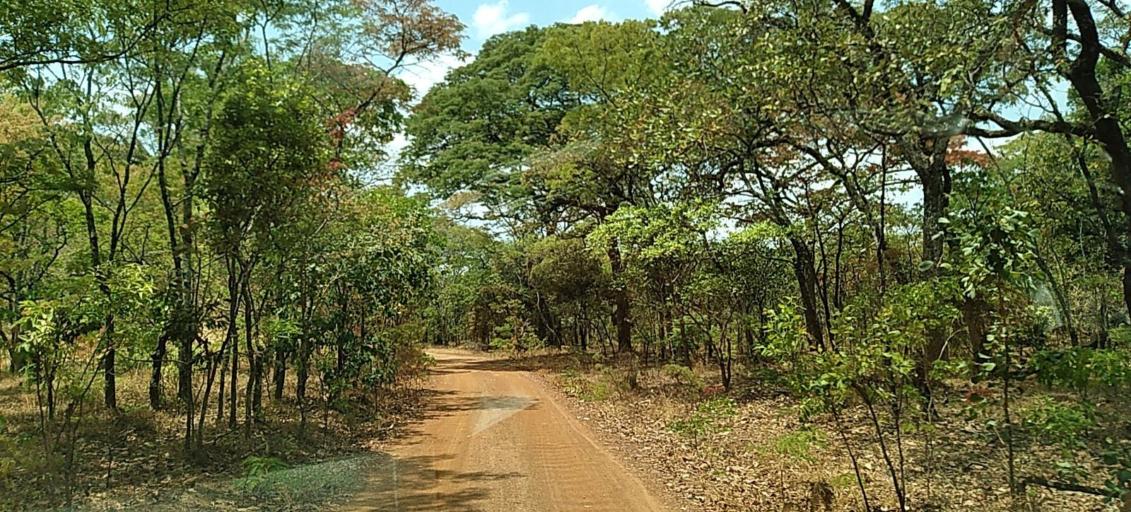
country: ZM
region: Copperbelt
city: Chililabombwe
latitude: -12.5001
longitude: 27.6397
